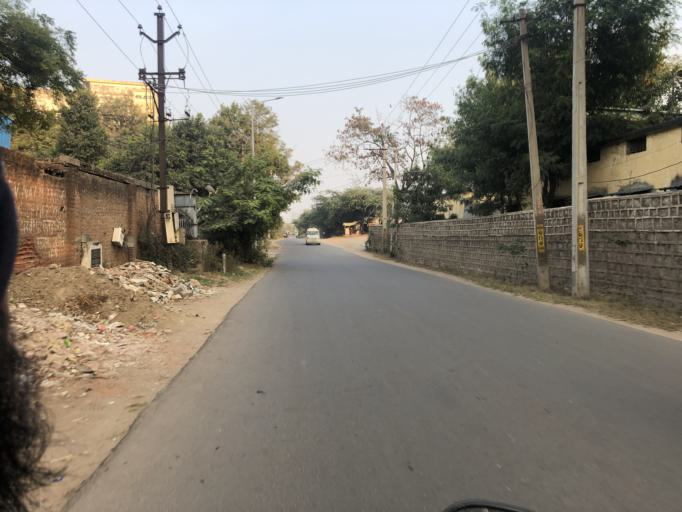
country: IN
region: Telangana
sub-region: Rangareddi
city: Kukatpalli
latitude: 17.4625
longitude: 78.4390
